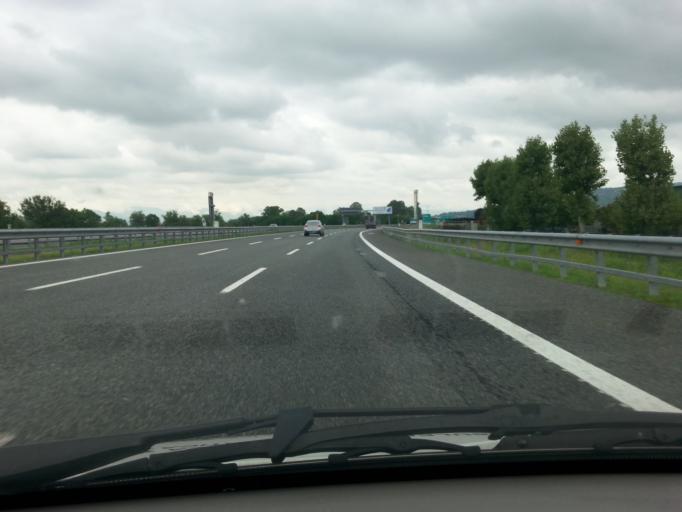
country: IT
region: Piedmont
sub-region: Provincia di Torino
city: La Loggia
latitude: 44.9613
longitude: 7.7057
